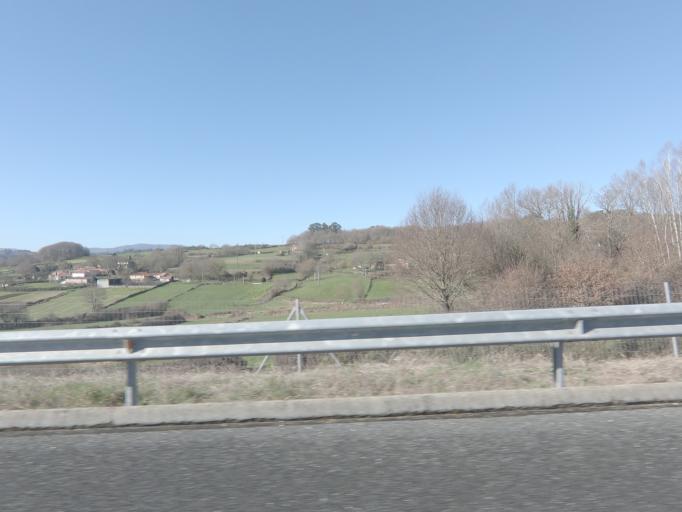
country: ES
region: Galicia
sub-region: Provincia de Pontevedra
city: Lalin
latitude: 42.6447
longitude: -8.1325
